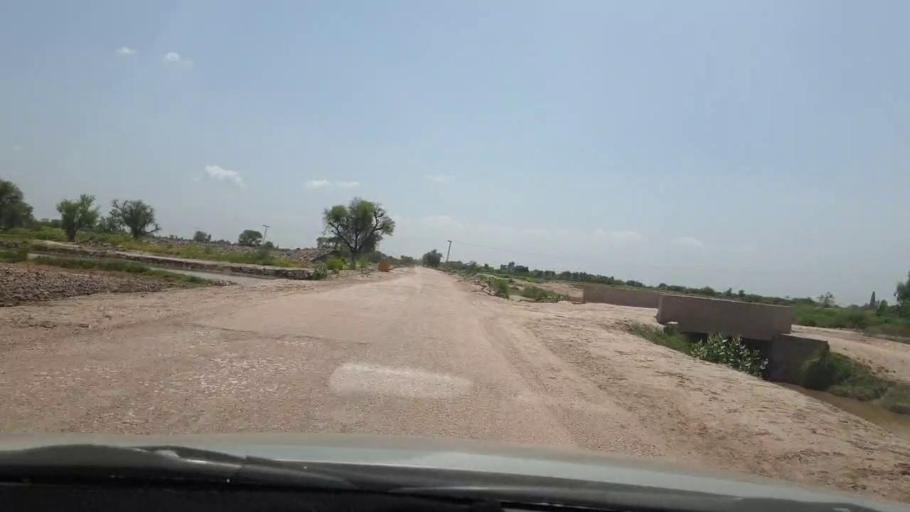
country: PK
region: Sindh
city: Pano Aqil
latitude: 27.7208
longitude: 69.1744
